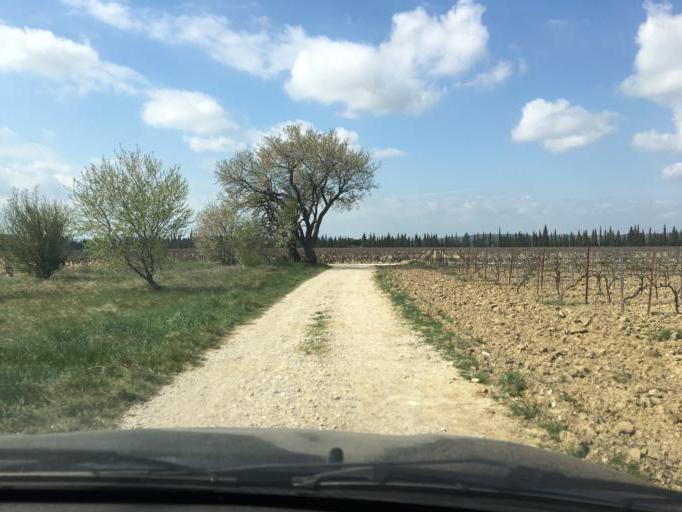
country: FR
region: Provence-Alpes-Cote d'Azur
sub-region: Departement du Vaucluse
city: Serignan-du-Comtat
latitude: 44.1726
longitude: 4.8213
